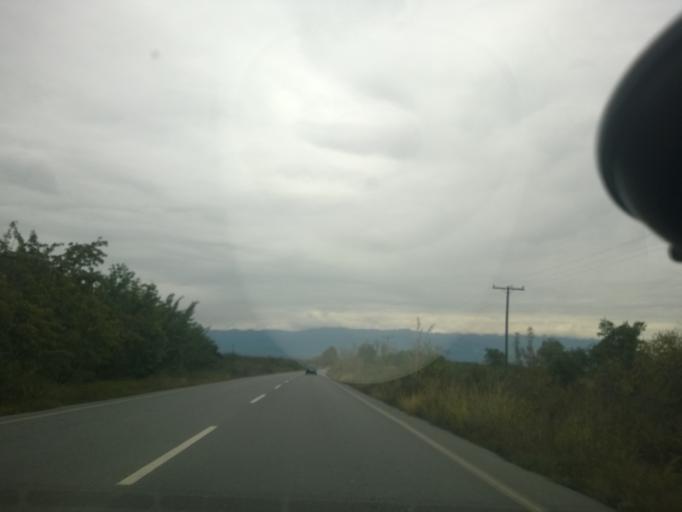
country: GR
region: Central Macedonia
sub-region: Nomos Pellis
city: Loutraki
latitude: 40.9720
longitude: 21.9629
